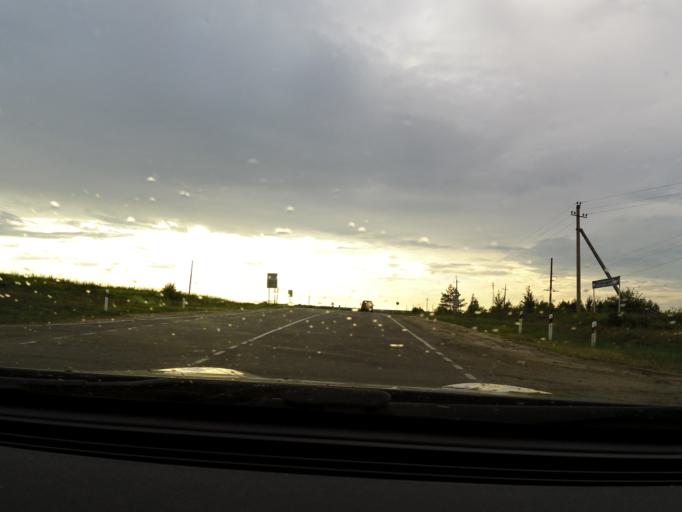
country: RU
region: Vladimir
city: Stavrovo
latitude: 56.1226
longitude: 40.0005
